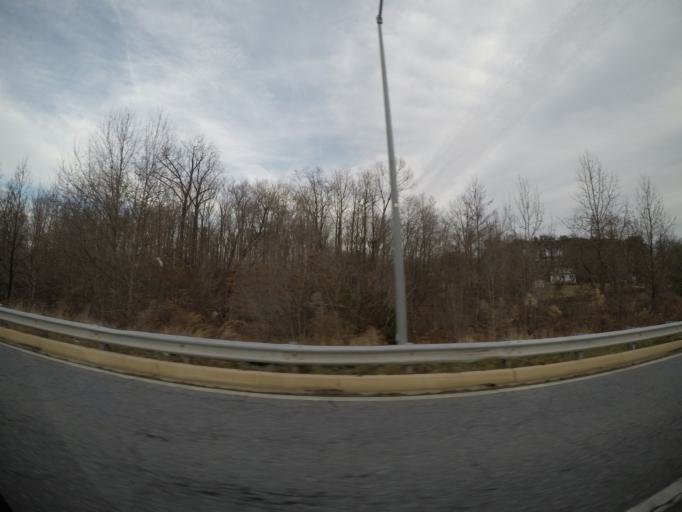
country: US
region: Maryland
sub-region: Howard County
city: Hanover
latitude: 39.1762
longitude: -76.7377
